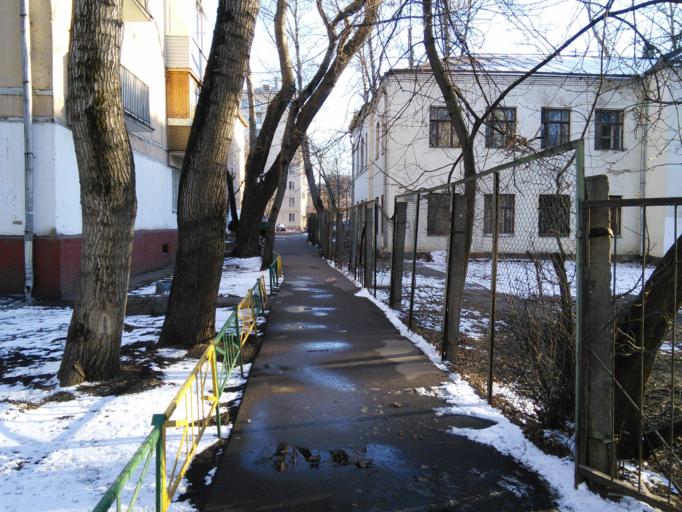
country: RU
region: Moscow
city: Mar'ina Roshcha
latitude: 55.7963
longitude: 37.6143
